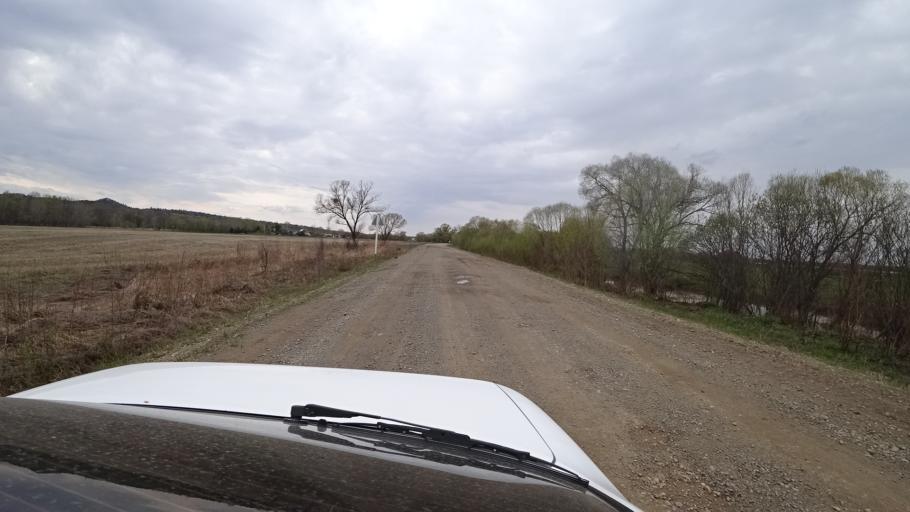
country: RU
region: Primorskiy
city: Novopokrovka
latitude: 45.4906
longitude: 134.4566
